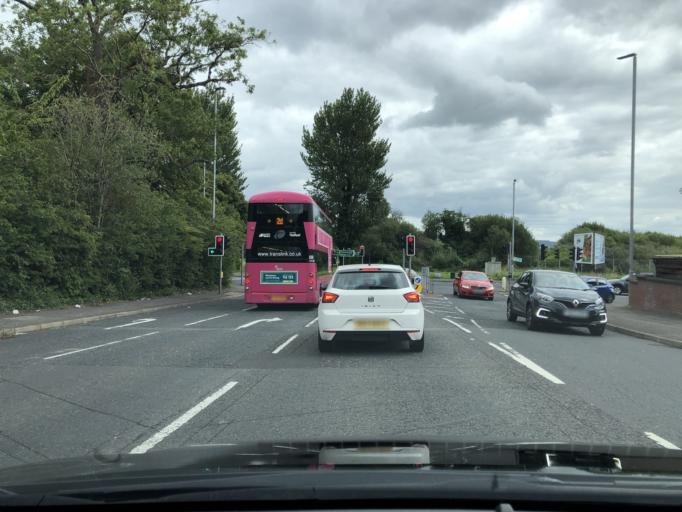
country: GB
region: Northern Ireland
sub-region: Newtownabbey District
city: Newtownabbey
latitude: 54.6549
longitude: -5.9131
